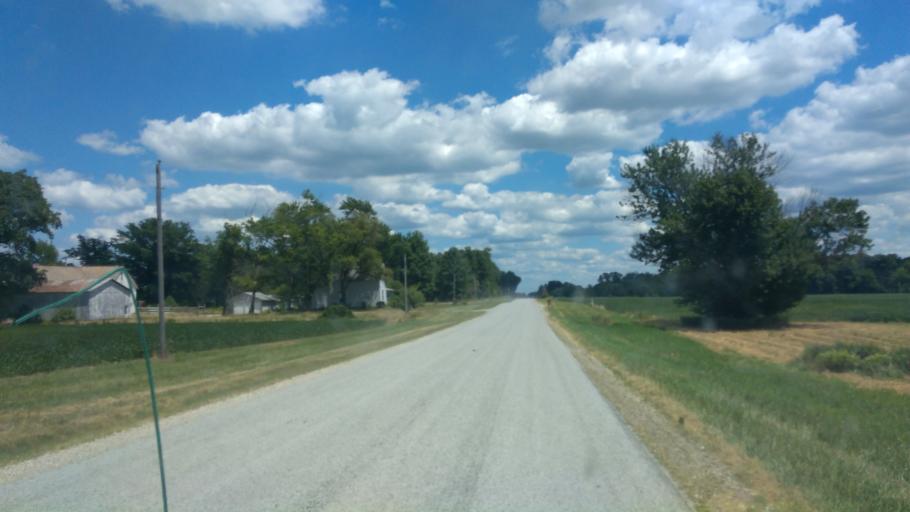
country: US
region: Indiana
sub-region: Adams County
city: Geneva
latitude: 40.5909
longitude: -85.0194
